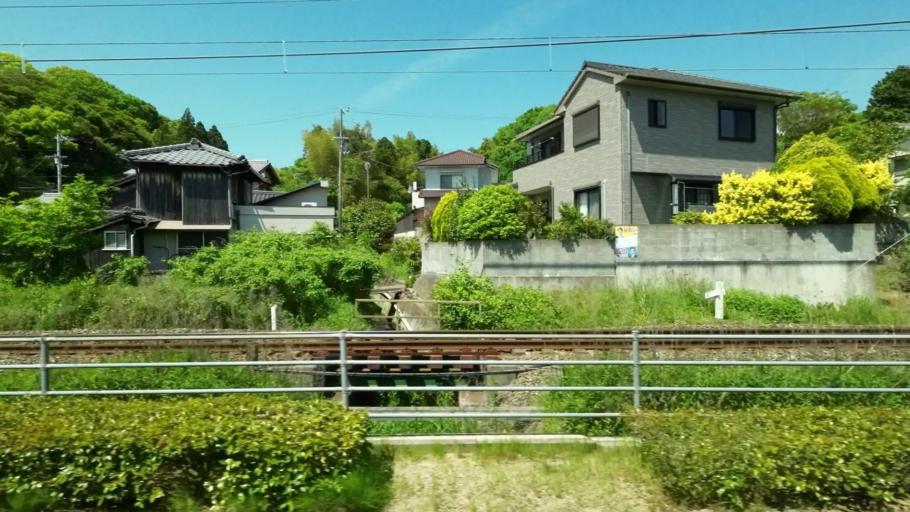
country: JP
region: Ehime
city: Hojo
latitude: 34.0807
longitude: 132.9848
